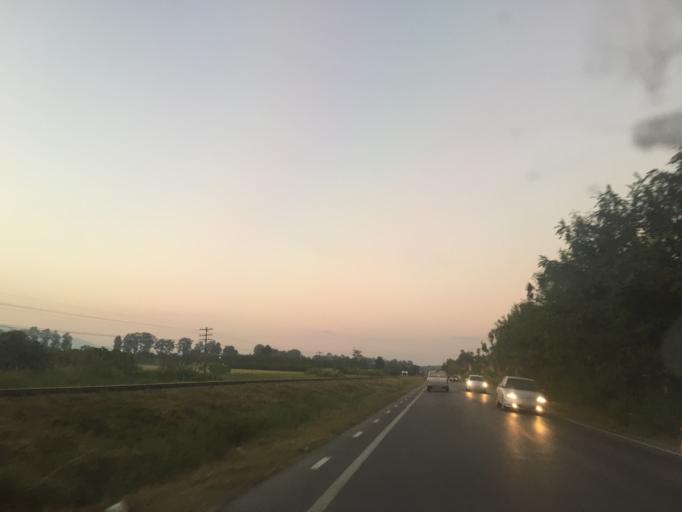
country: TH
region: Chiang Mai
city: Saraphi
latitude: 18.6637
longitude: 99.0446
